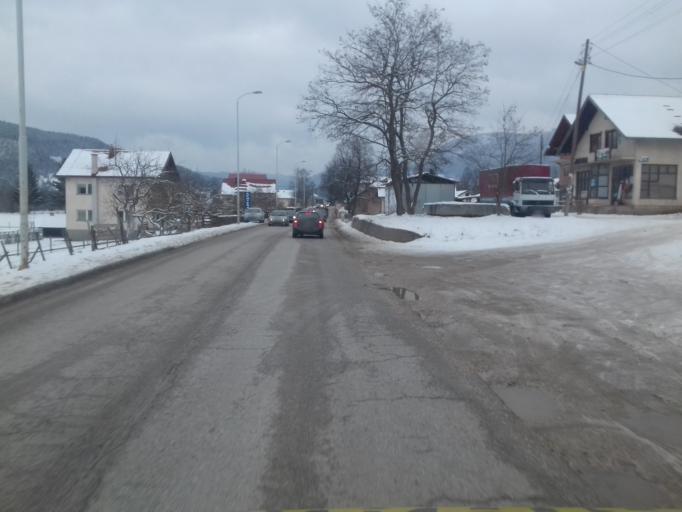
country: BA
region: Republika Srpska
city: Pale
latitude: 43.8792
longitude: 18.6055
